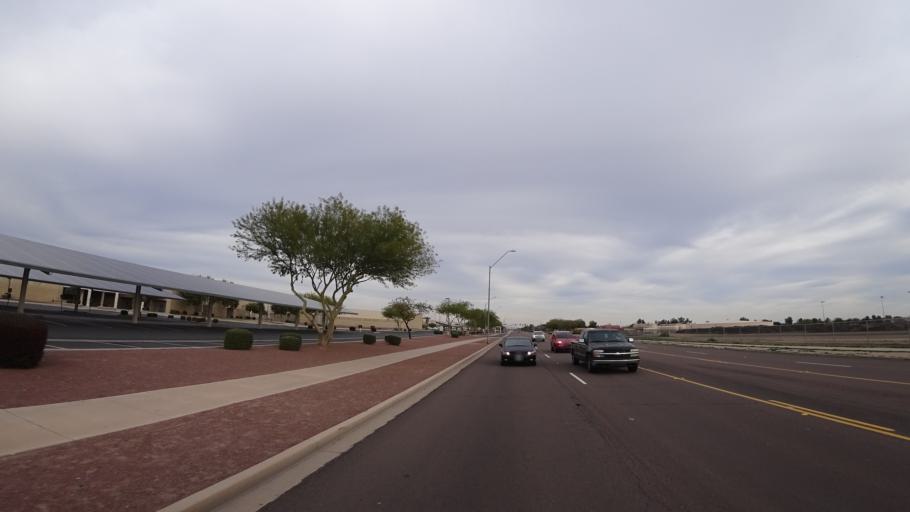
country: US
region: Arizona
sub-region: Maricopa County
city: Surprise
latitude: 33.6241
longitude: -112.3884
